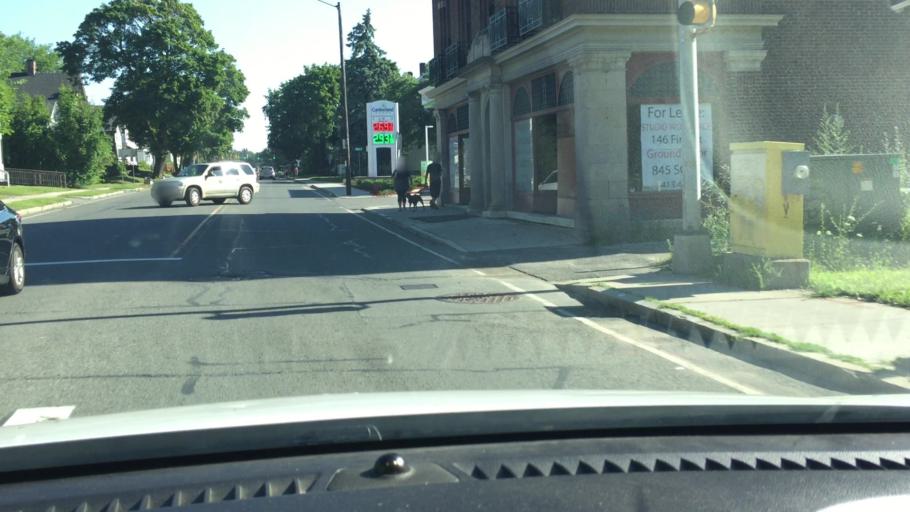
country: US
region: Massachusetts
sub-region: Berkshire County
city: Pittsfield
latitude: 42.4525
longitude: -73.2500
